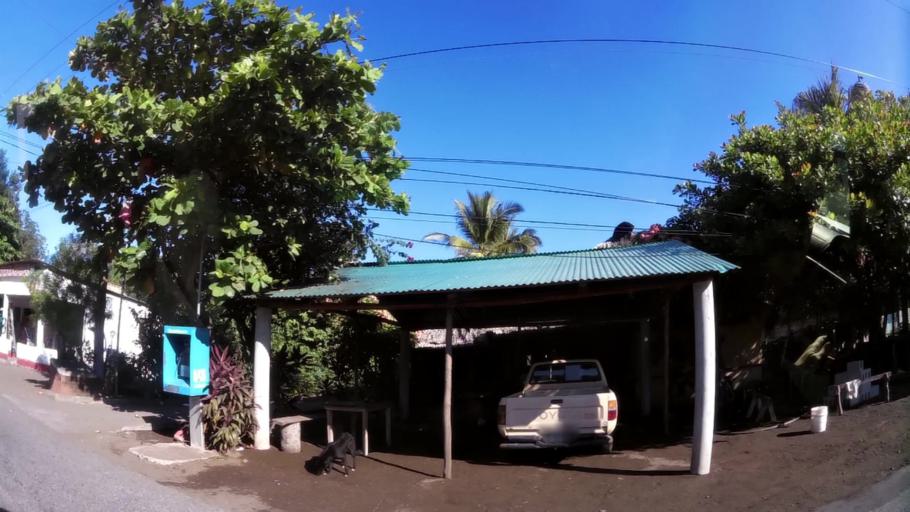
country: GT
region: Santa Rosa
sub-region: Municipio de Taxisco
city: Taxisco
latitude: 13.8970
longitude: -90.4899
